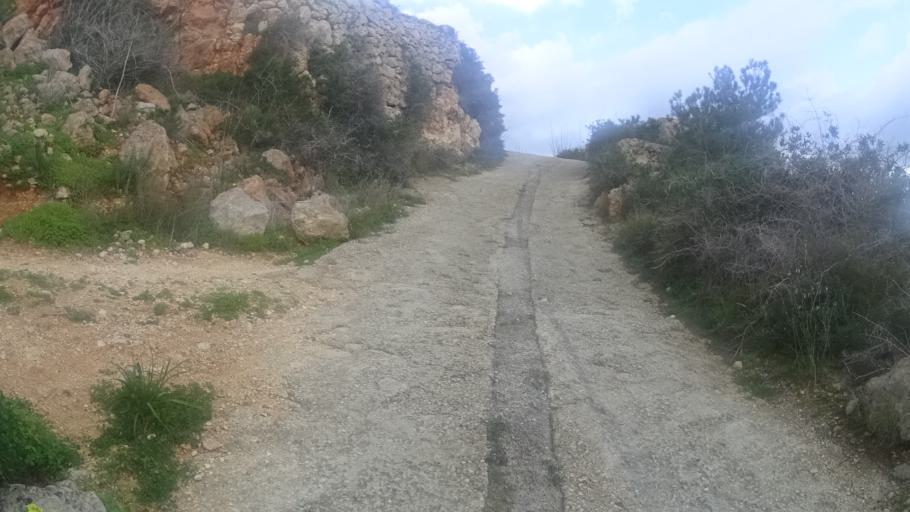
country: MT
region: L-Imtarfa
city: Imtarfa
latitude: 35.8945
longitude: 14.3744
